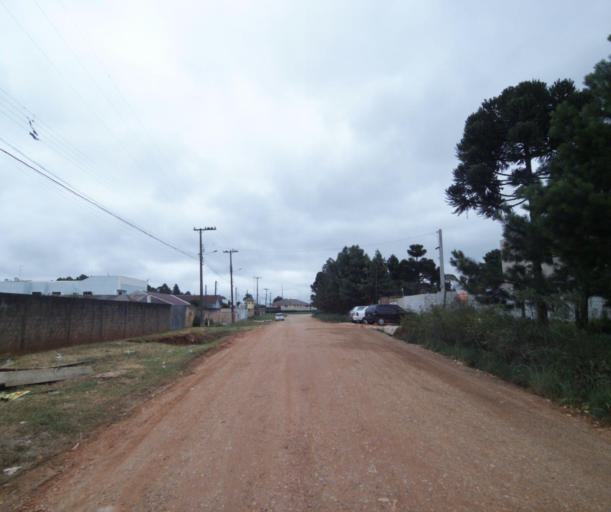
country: BR
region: Parana
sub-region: Quatro Barras
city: Quatro Barras
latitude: -25.3619
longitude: -49.1140
